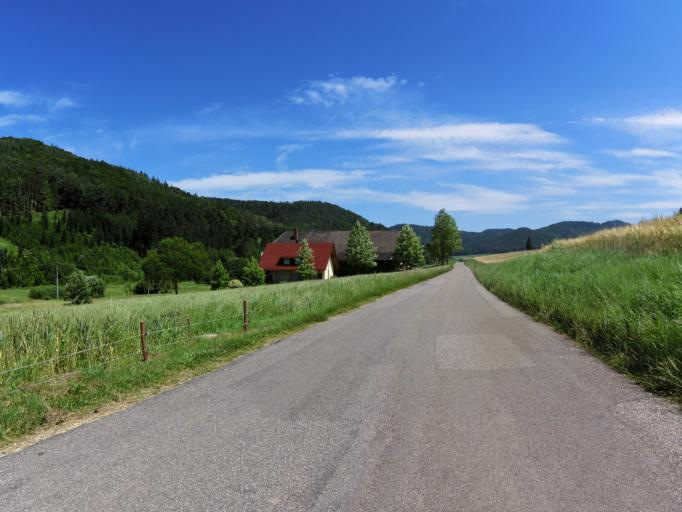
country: DE
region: Baden-Wuerttemberg
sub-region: Freiburg Region
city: Hohberg
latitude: 48.2961
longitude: 7.9163
